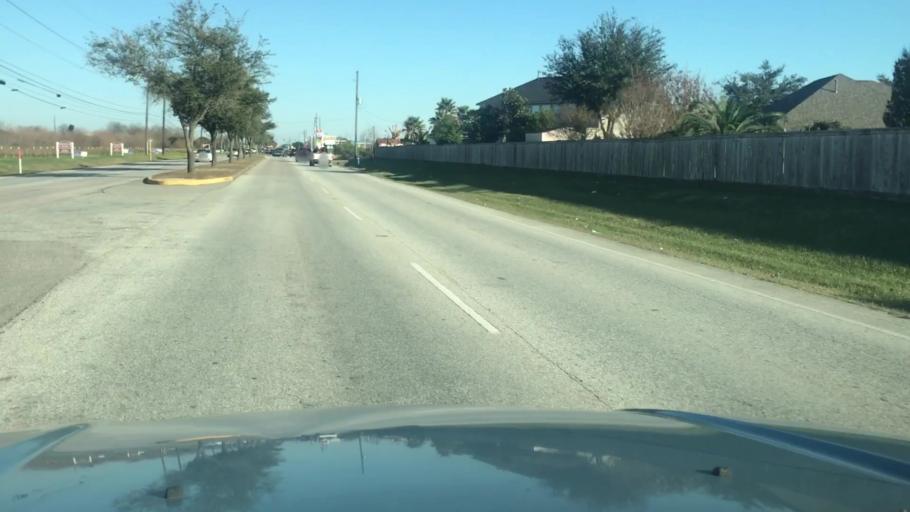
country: US
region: Texas
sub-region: Fort Bend County
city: Cinco Ranch
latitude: 29.8312
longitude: -95.7240
